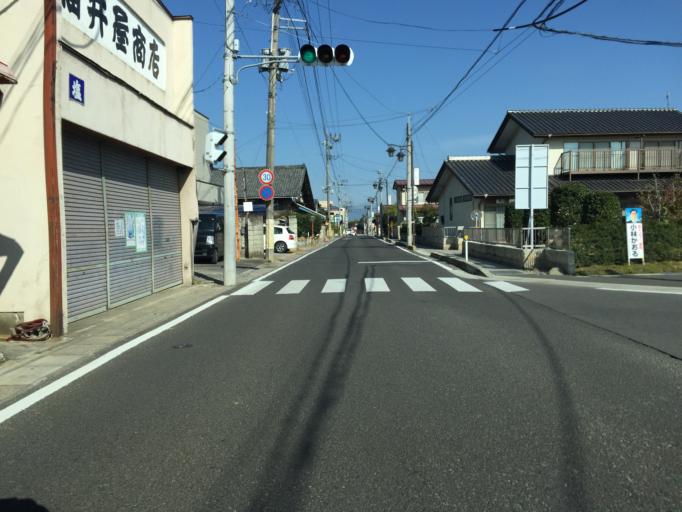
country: JP
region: Fukushima
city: Fukushima-shi
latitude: 37.7271
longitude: 140.4383
